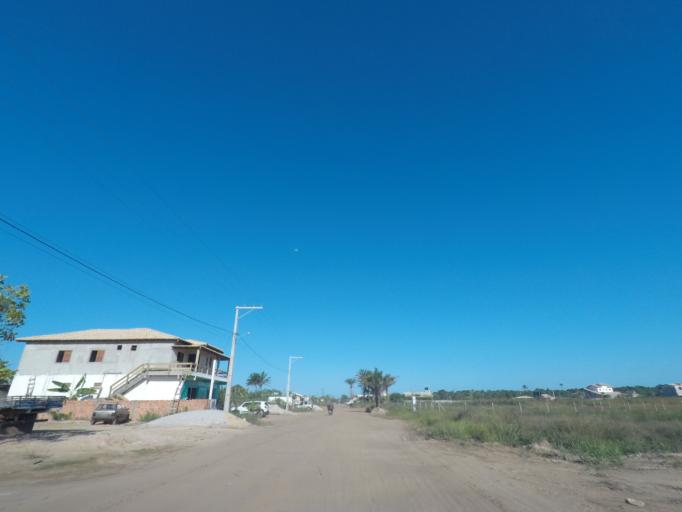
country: BR
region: Bahia
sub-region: Camamu
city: Camamu
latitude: -13.9320
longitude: -38.9405
